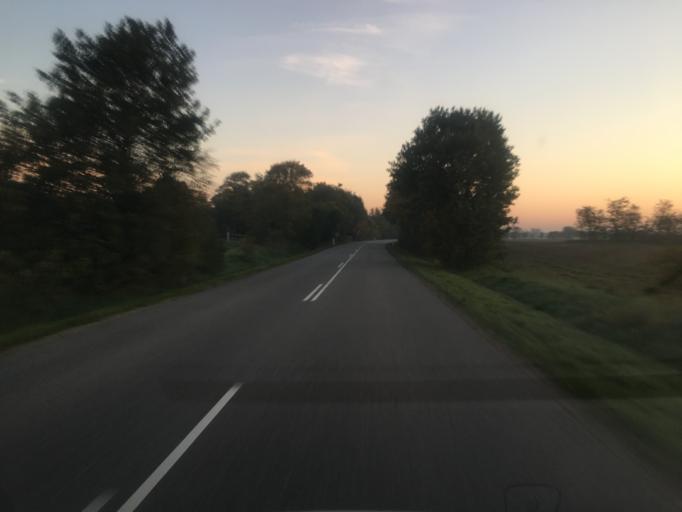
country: DE
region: Schleswig-Holstein
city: Bramstedtlund
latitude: 54.9679
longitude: 9.1202
